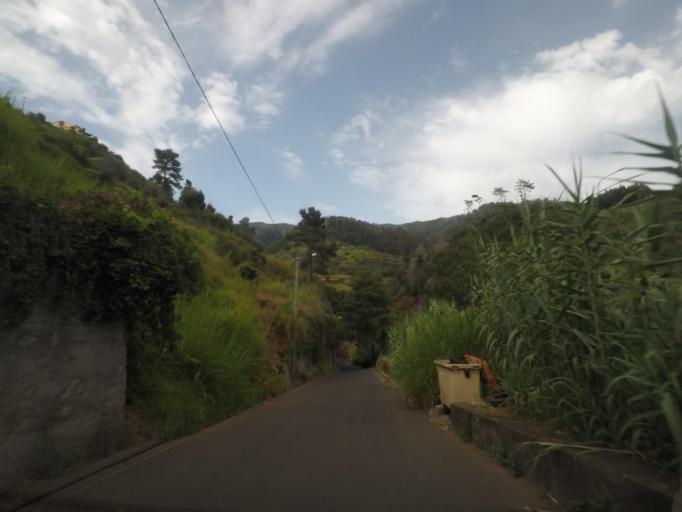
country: PT
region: Madeira
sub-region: Calheta
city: Arco da Calheta
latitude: 32.7325
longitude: -17.1530
